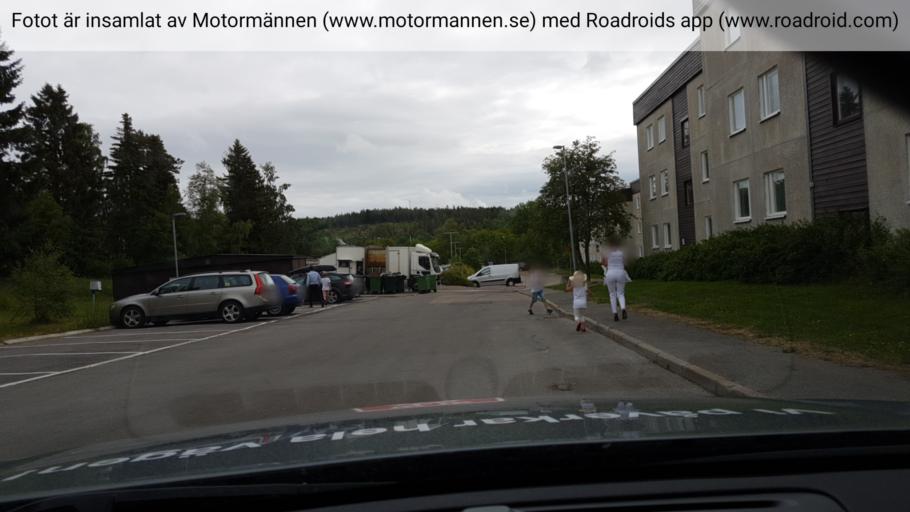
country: SE
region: Vaesternorrland
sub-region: Sundsvalls Kommun
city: Johannedal
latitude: 62.4206
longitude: 17.3397
